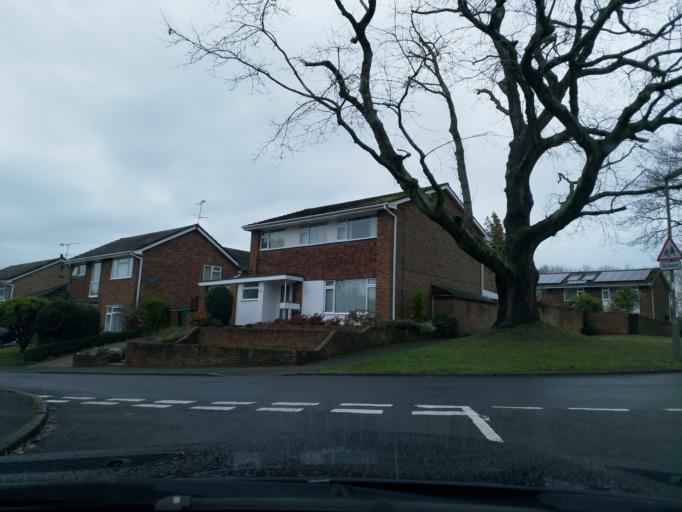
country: GB
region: England
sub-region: Surrey
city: Frimley
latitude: 51.3180
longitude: -0.7234
